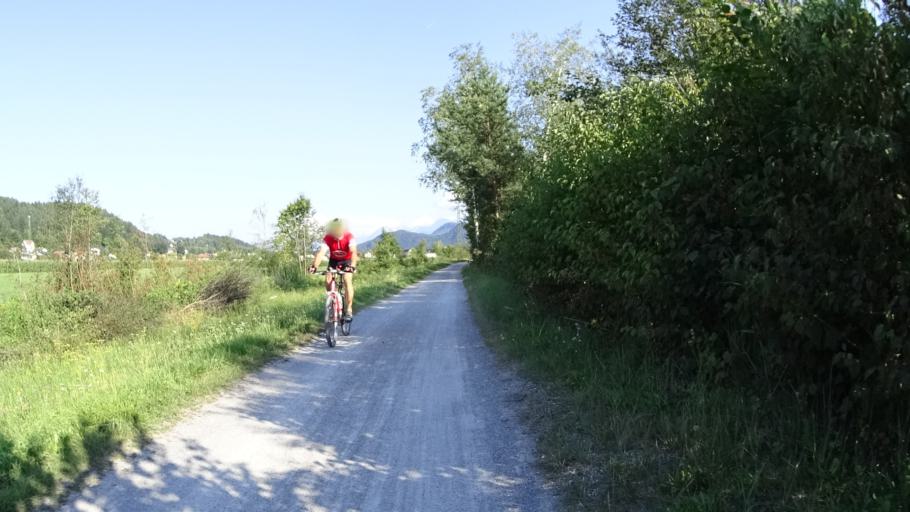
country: AT
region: Carinthia
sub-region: Politischer Bezirk Villach Land
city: Wernberg
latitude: 46.6103
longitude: 13.9356
